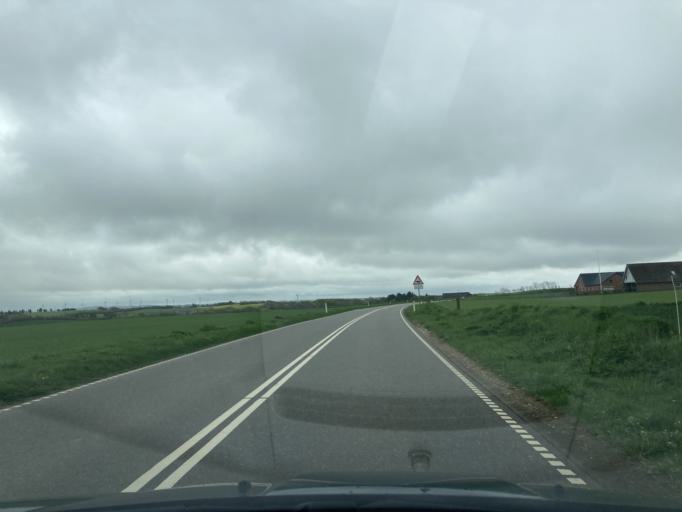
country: DK
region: North Denmark
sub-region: Thisted Kommune
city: Hurup
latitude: 56.8295
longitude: 8.3593
